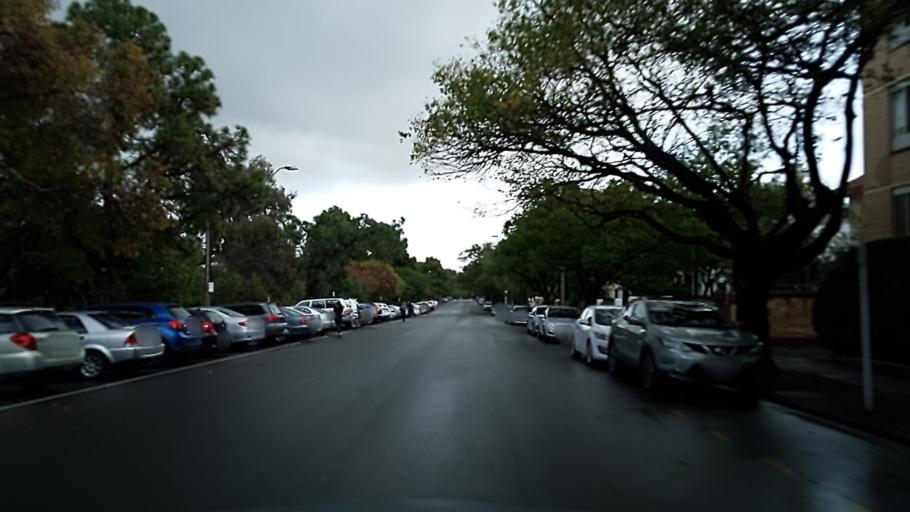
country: AU
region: South Australia
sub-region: Adelaide
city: North Adelaide
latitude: -34.9106
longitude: 138.5875
